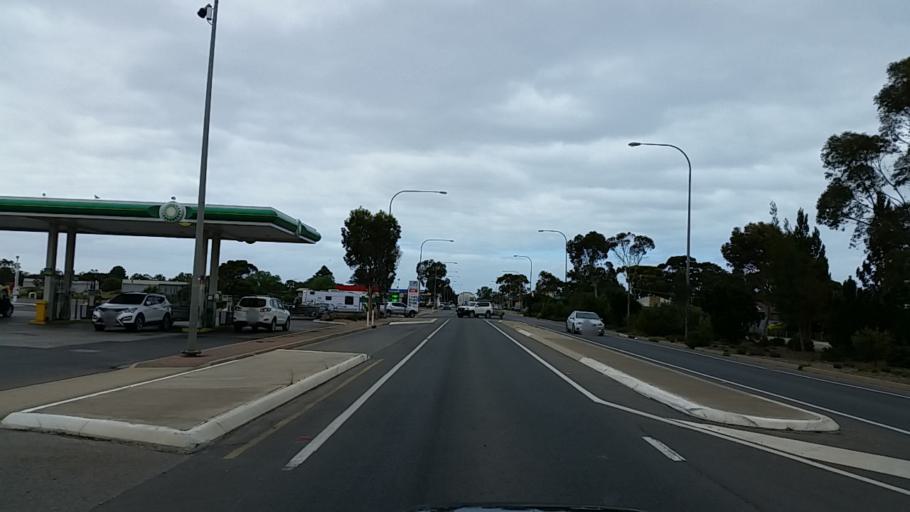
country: AU
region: South Australia
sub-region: Wakefield
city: Balaklava
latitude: -34.1806
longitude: 138.1539
